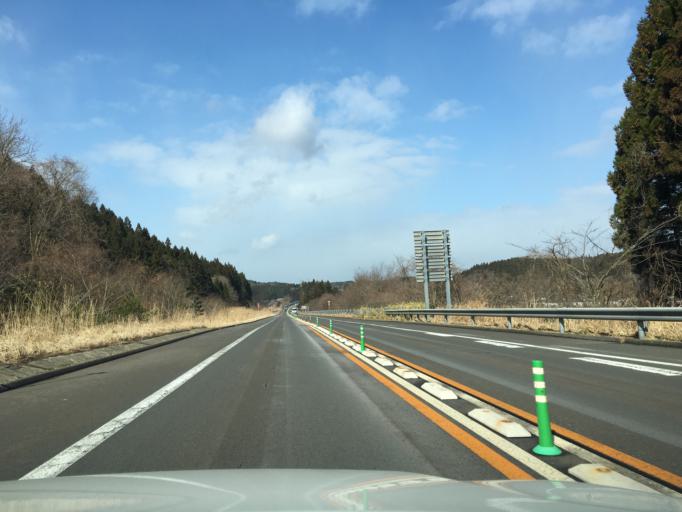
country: JP
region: Akita
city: Akita
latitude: 39.7514
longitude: 140.1475
